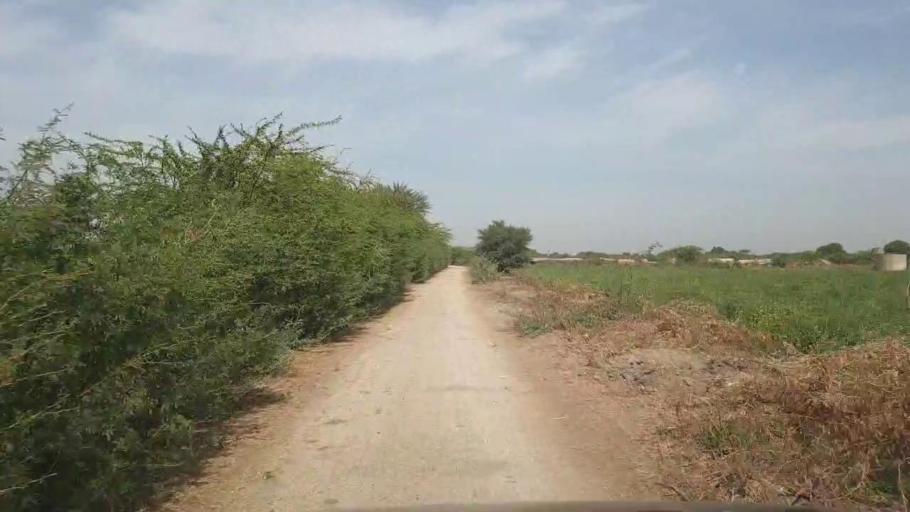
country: PK
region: Sindh
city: Kunri
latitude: 25.2397
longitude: 69.6768
